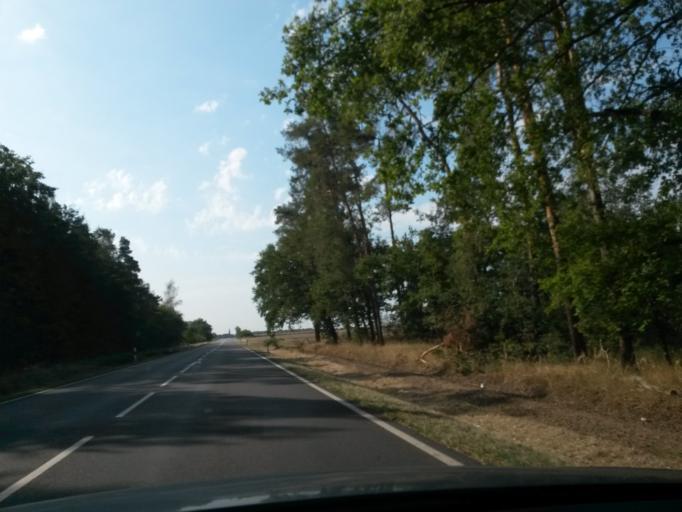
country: DE
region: Saxony-Anhalt
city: Jerichow
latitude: 52.5282
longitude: 12.0159
